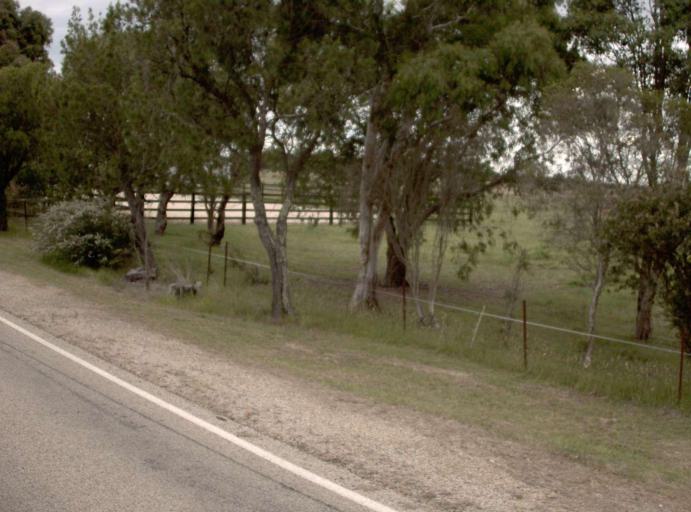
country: AU
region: Victoria
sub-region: East Gippsland
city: Bairnsdale
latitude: -37.8671
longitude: 147.5620
